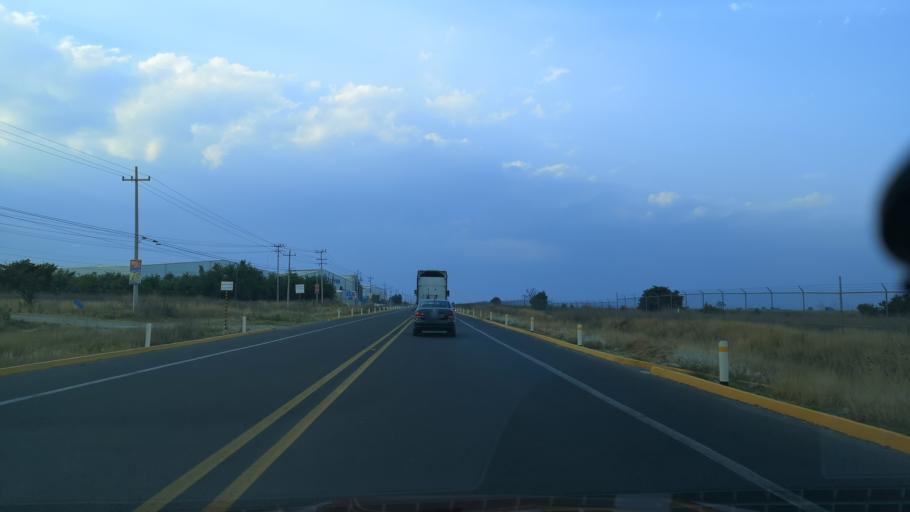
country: MX
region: Puebla
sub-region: Juan C. Bonilla
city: Santa Maria Zacatepec
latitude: 19.1403
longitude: -98.3739
